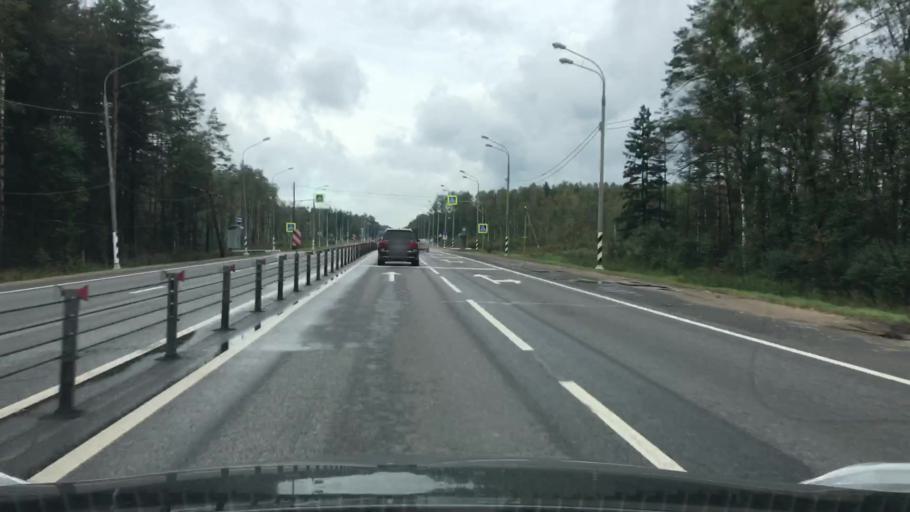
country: RU
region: Moskovskaya
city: Reshetnikovo
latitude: 56.4002
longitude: 36.6535
